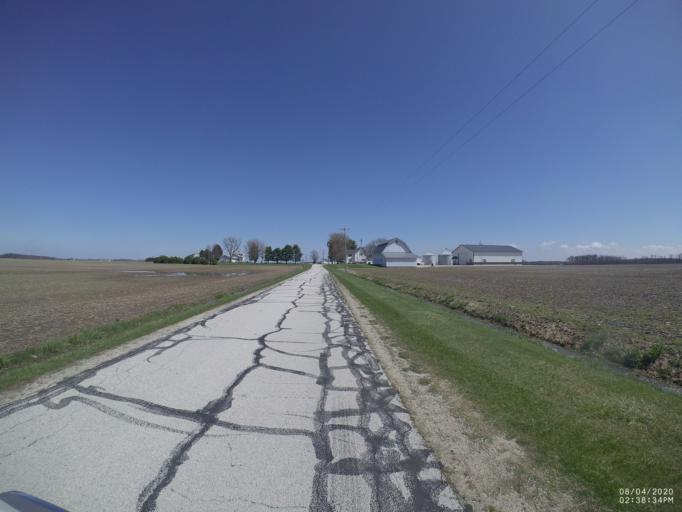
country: US
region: Ohio
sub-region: Sandusky County
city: Gibsonburg
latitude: 41.2795
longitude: -83.3009
